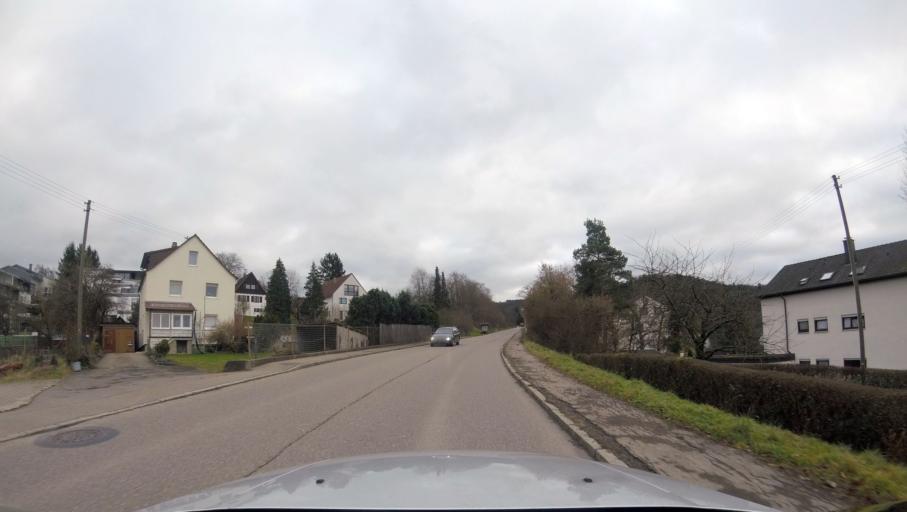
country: DE
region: Baden-Wuerttemberg
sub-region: Regierungsbezirk Stuttgart
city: Allmersbach im Tal
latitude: 48.9050
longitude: 9.4728
